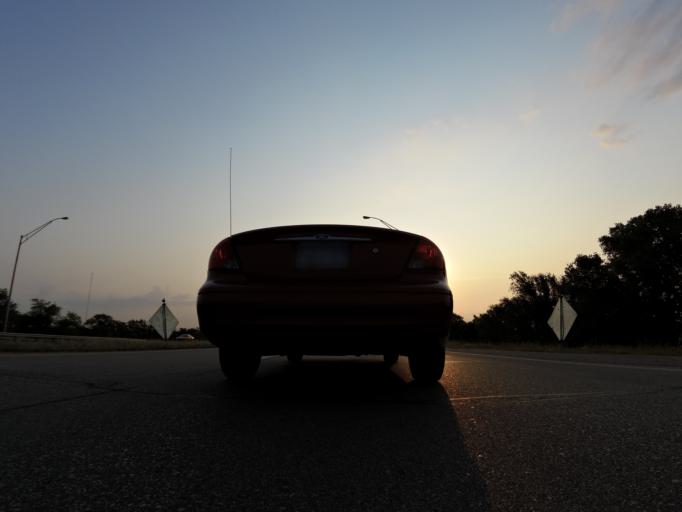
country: US
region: Kansas
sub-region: Sedgwick County
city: Park City
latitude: 37.7576
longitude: -97.3347
